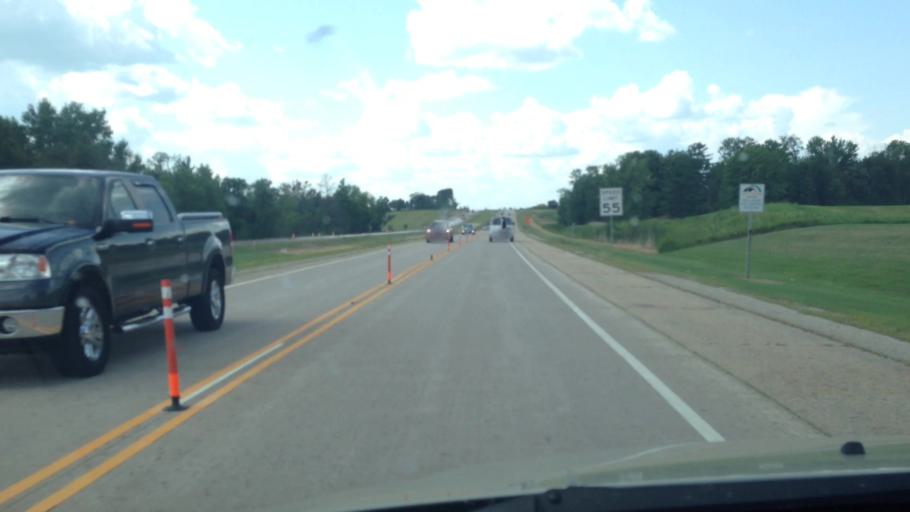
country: US
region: Wisconsin
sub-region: Brown County
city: Pulaski
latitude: 44.6954
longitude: -88.3457
